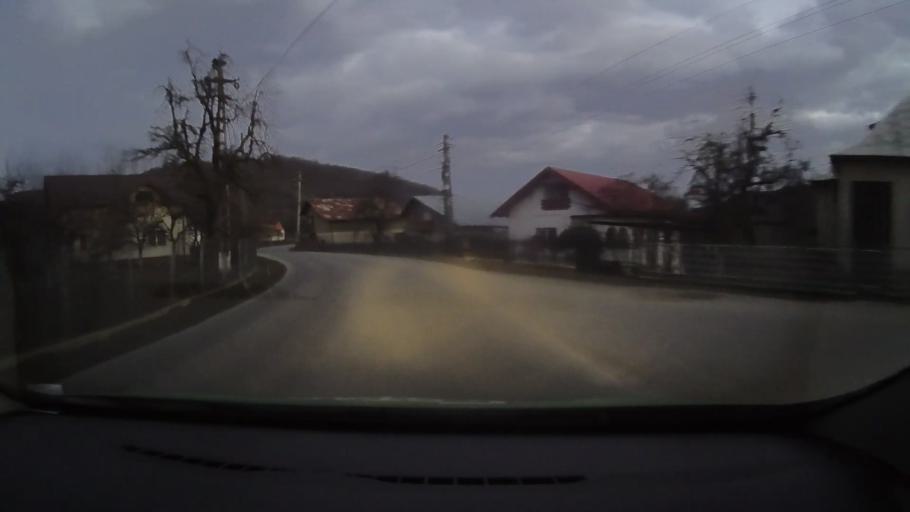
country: RO
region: Prahova
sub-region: Comuna Provita de Jos
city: Provita de Jos
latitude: 45.1295
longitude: 25.6474
